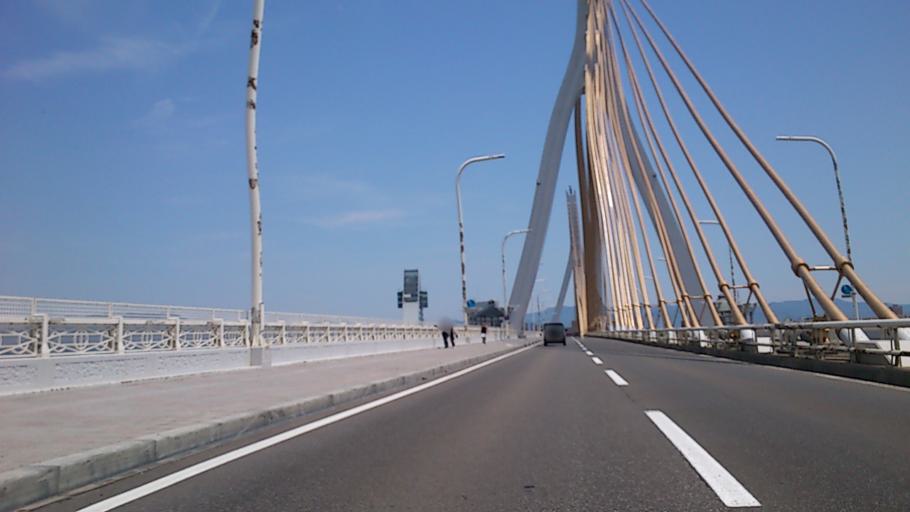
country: JP
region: Aomori
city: Aomori Shi
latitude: 40.8311
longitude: 140.7339
